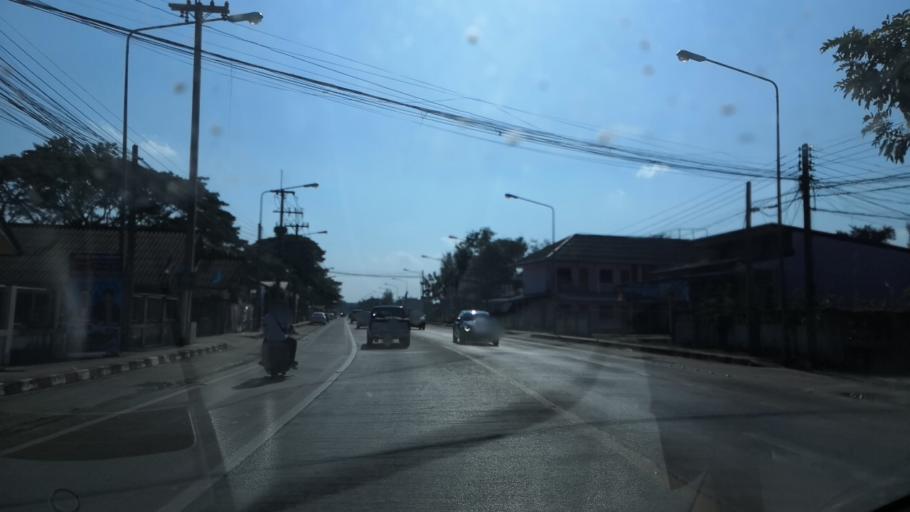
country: TH
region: Chiang Rai
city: Chiang Rai
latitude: 19.9334
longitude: 99.8410
